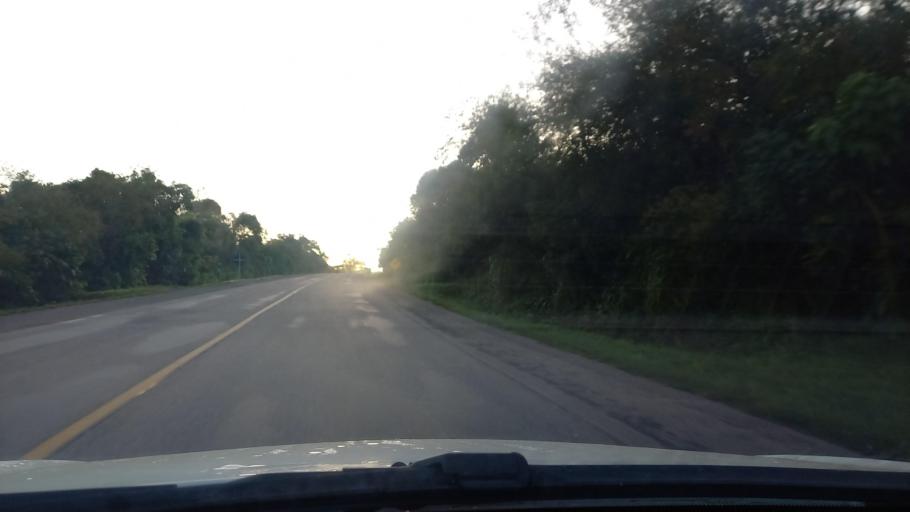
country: BR
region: Rio Grande do Sul
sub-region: Candelaria
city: Candelaria
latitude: -29.6837
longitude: -52.8448
